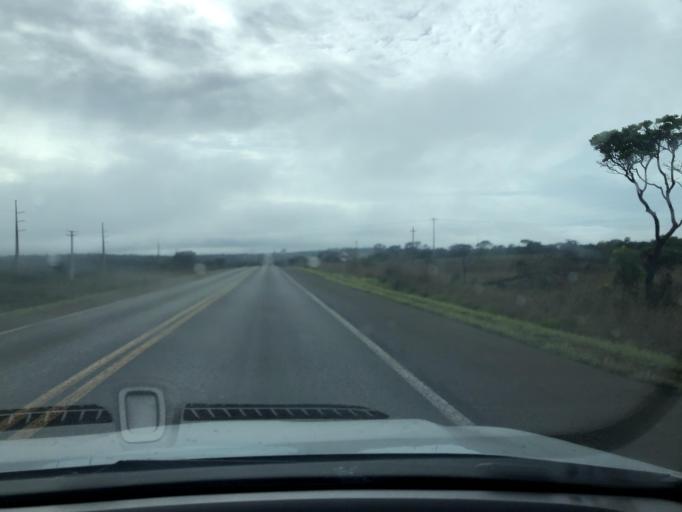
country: BR
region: Goias
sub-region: Cristalina
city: Cristalina
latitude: -16.7221
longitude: -47.6480
